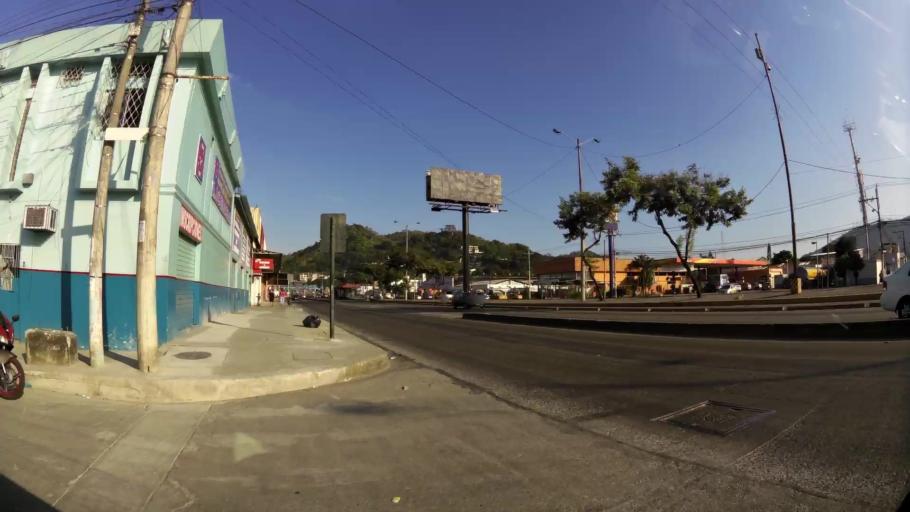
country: EC
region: Guayas
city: Guayaquil
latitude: -2.1574
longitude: -79.9291
